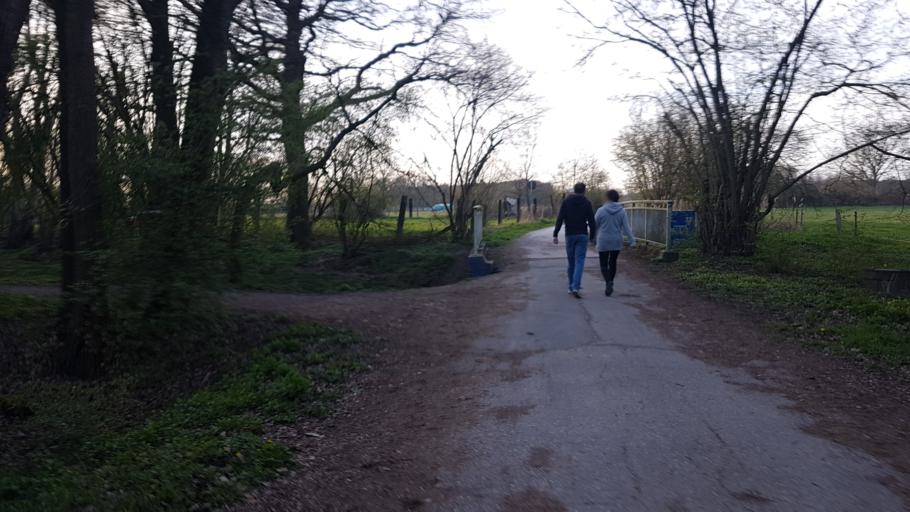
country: DE
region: Lower Saxony
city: Isernhagen Farster Bauerschaft
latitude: 52.4418
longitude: 9.8527
